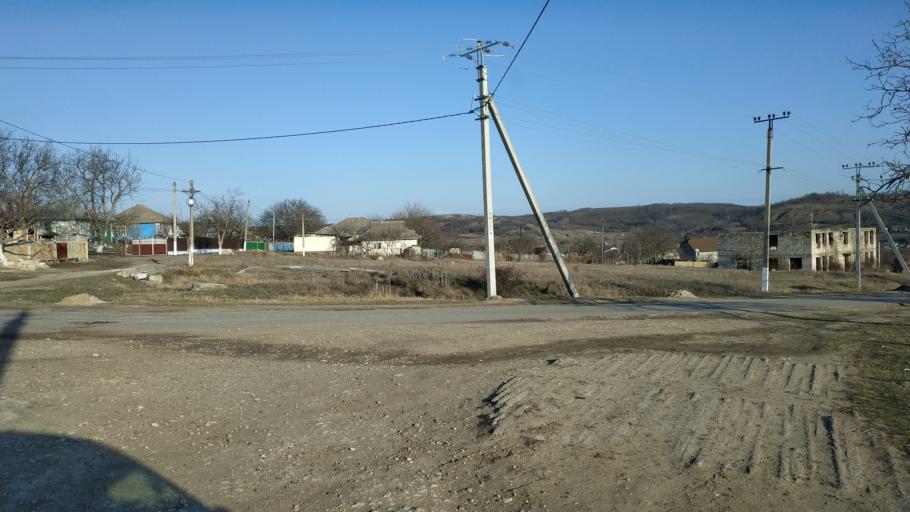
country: MD
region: Hincesti
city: Hincesti
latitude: 46.7012
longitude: 28.5419
